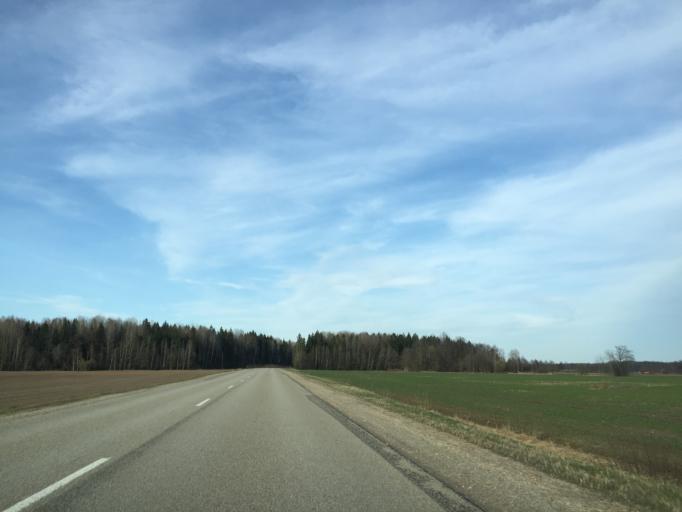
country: LV
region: Lielvarde
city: Lielvarde
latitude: 56.7890
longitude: 24.8038
